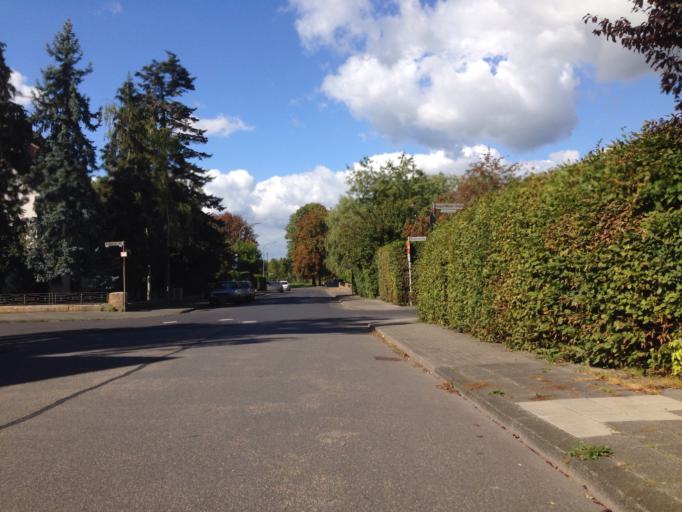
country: DE
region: Hesse
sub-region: Regierungsbezirk Giessen
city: Giessen
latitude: 50.5903
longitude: 8.6932
